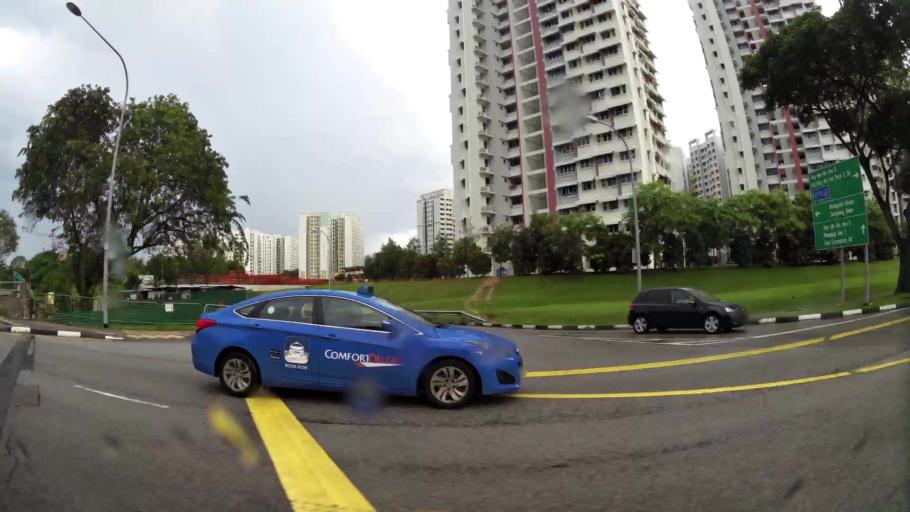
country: MY
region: Johor
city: Kampung Pasir Gudang Baru
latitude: 1.3803
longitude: 103.8768
